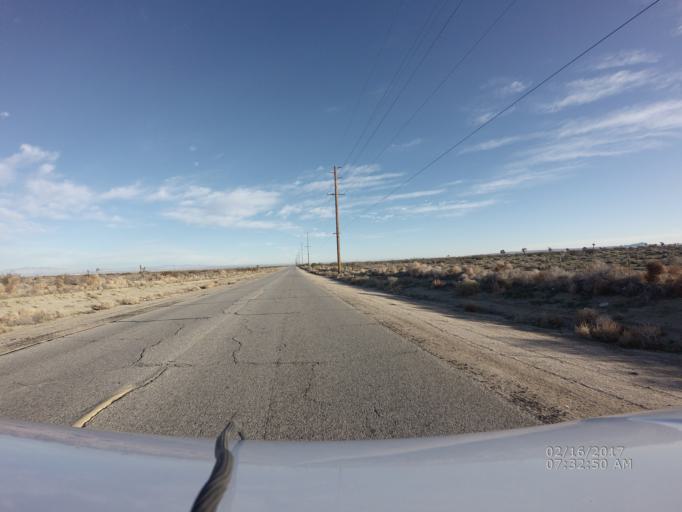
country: US
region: California
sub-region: Los Angeles County
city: Littlerock
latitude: 34.6376
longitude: -117.9696
